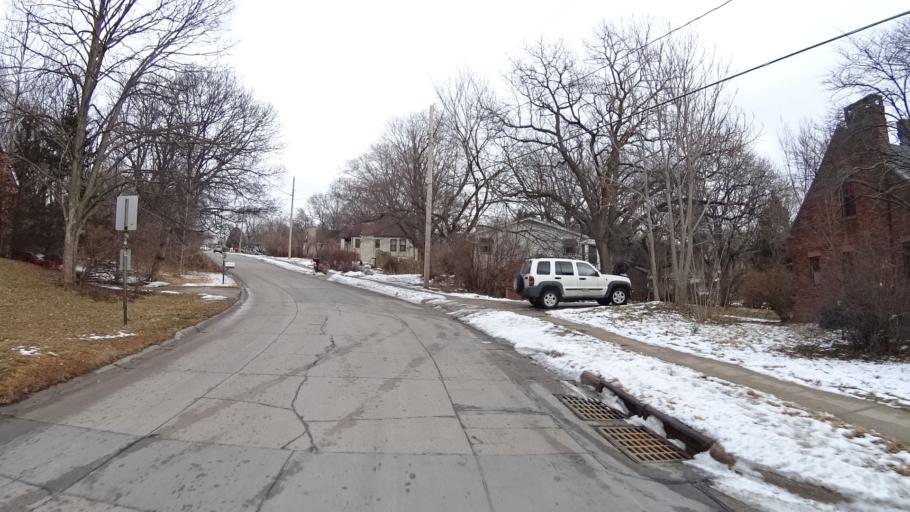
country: US
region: Nebraska
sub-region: Sarpy County
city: Bellevue
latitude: 41.1650
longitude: -95.9200
